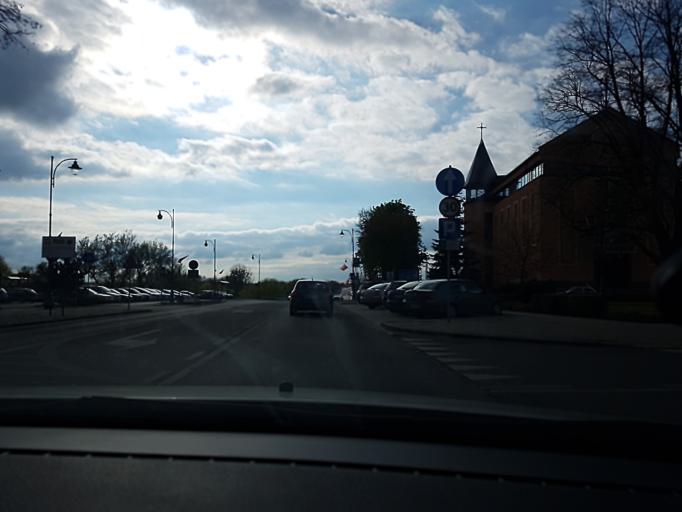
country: PL
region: Masovian Voivodeship
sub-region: Powiat sochaczewski
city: Sochaczew
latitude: 52.2294
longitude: 20.2375
